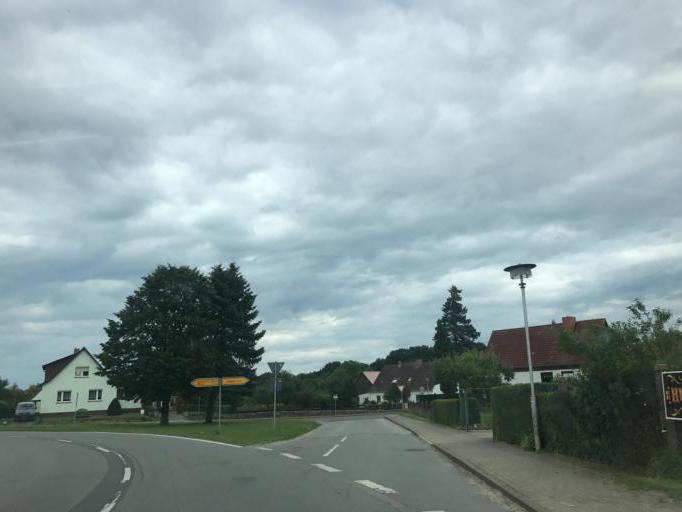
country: DE
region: Mecklenburg-Vorpommern
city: Rechlin
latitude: 53.2295
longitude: 12.7810
